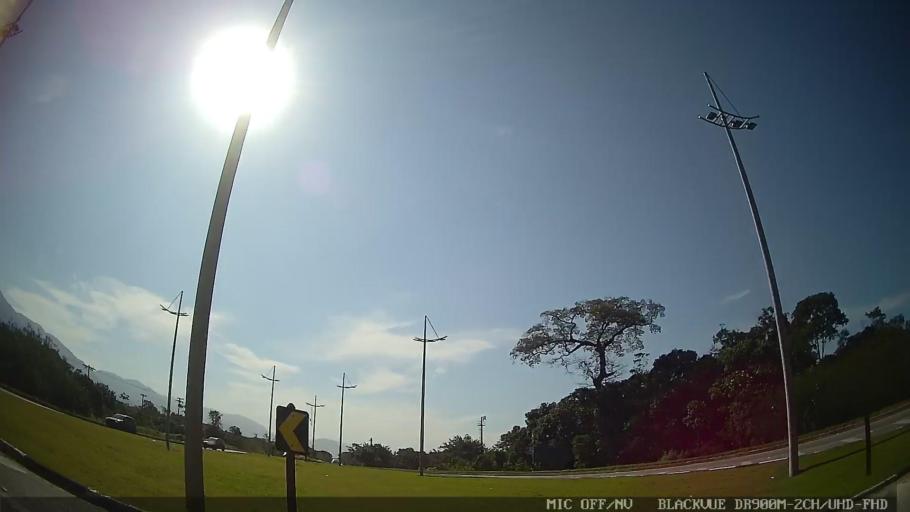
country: BR
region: Sao Paulo
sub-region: Bertioga
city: Bertioga
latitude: -23.8271
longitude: -46.1377
